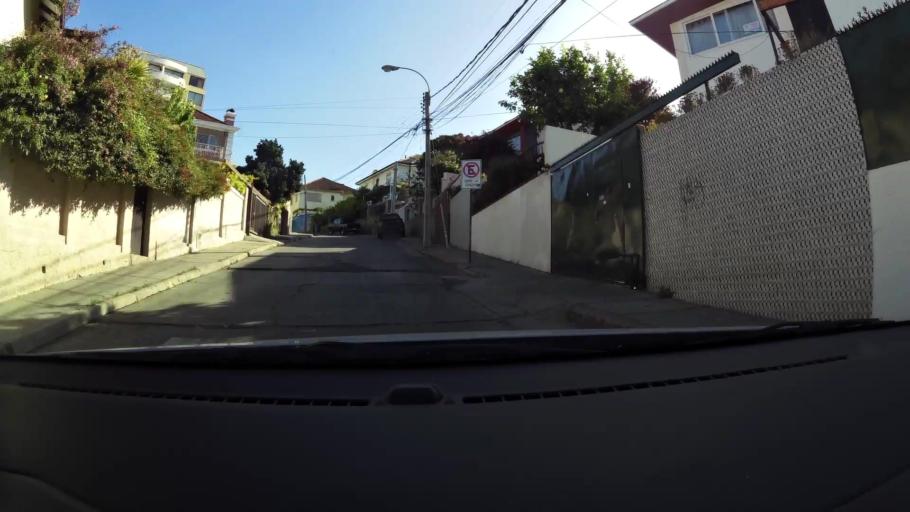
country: CL
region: Valparaiso
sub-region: Provincia de Valparaiso
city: Vina del Mar
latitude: -33.0275
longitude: -71.5603
